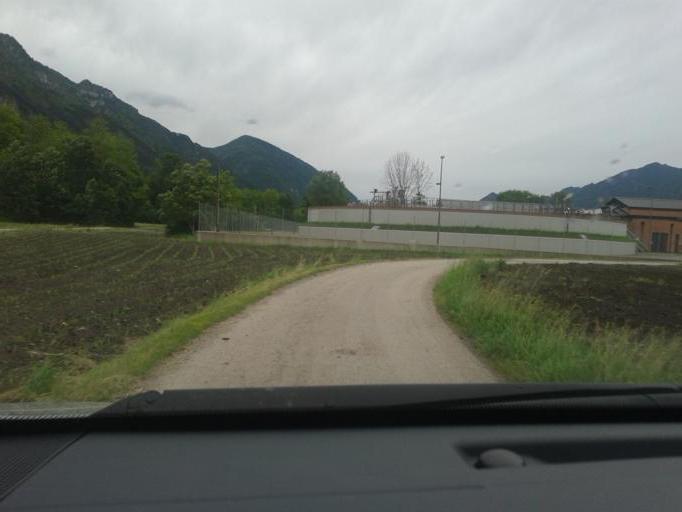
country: IT
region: Trentino-Alto Adige
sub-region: Provincia di Trento
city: Storo
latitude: 45.8401
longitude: 10.5594
